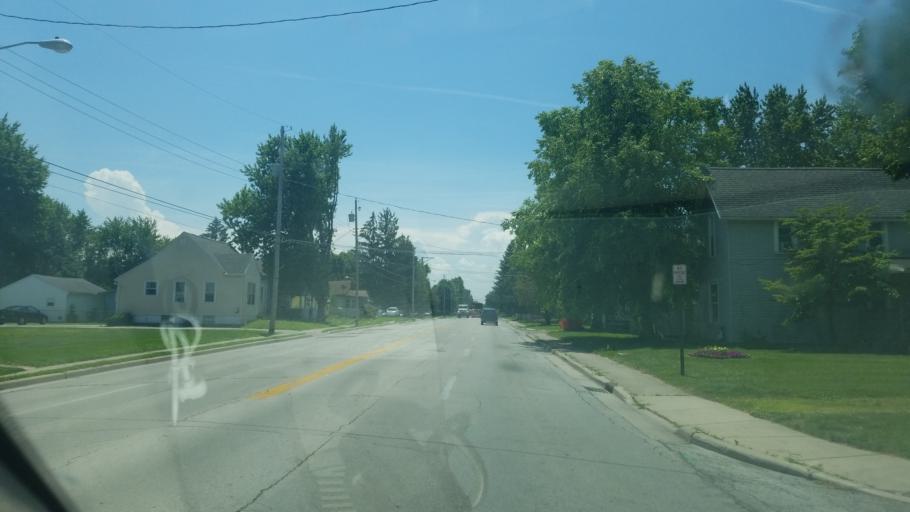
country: US
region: Ohio
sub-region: Hancock County
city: Findlay
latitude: 41.0290
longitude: -83.6412
